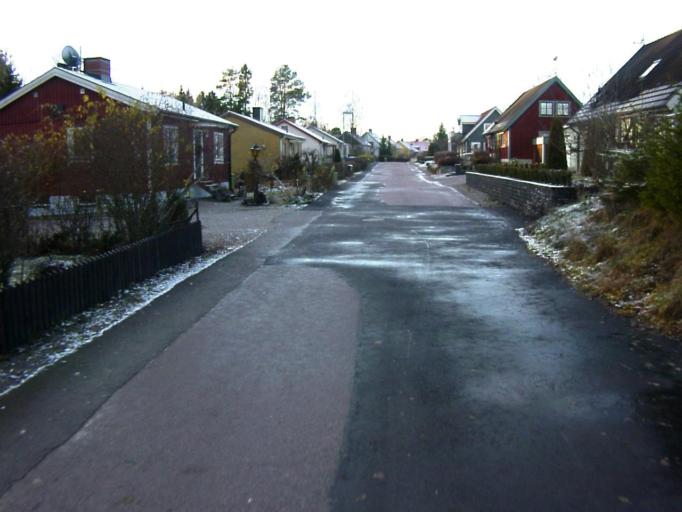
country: SE
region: Soedermanland
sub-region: Eskilstuna Kommun
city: Arla
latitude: 59.3174
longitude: 16.5976
